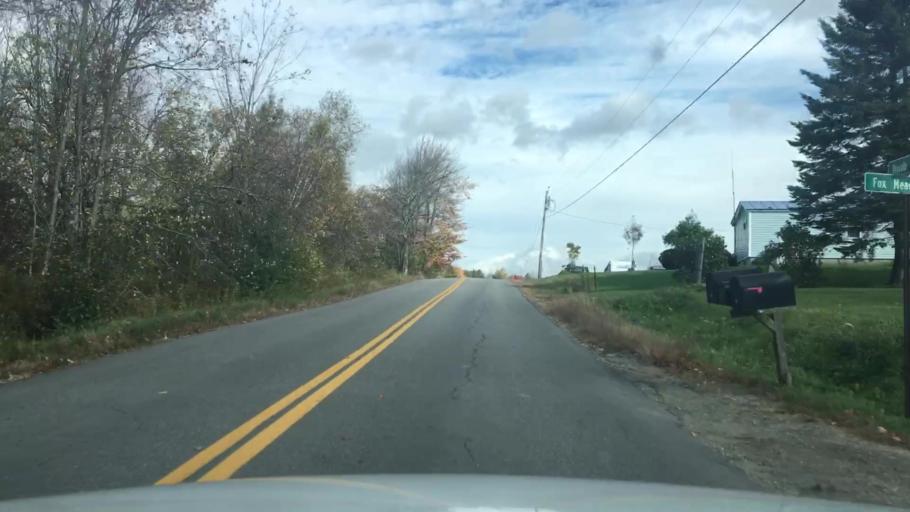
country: US
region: Maine
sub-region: Waldo County
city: Searsmont
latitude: 44.3673
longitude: -69.1466
